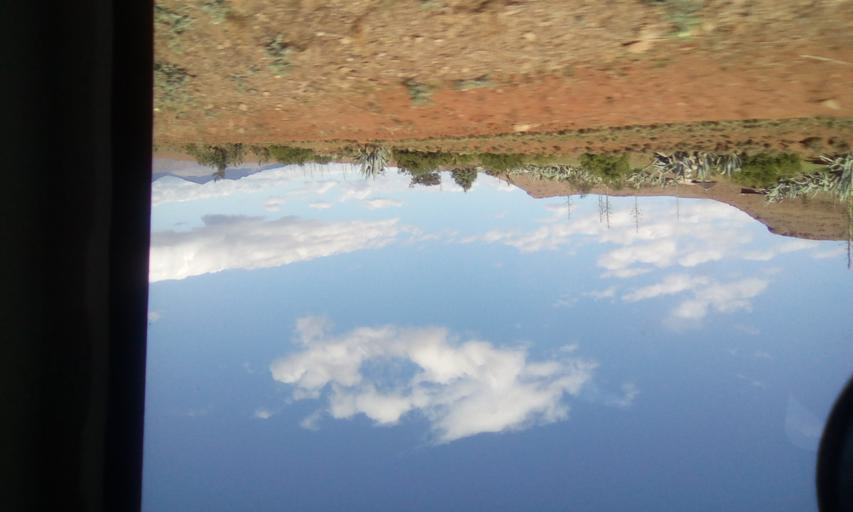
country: LS
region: Qacha's Nek
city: Qacha's Nek
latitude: -30.0476
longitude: 28.2830
